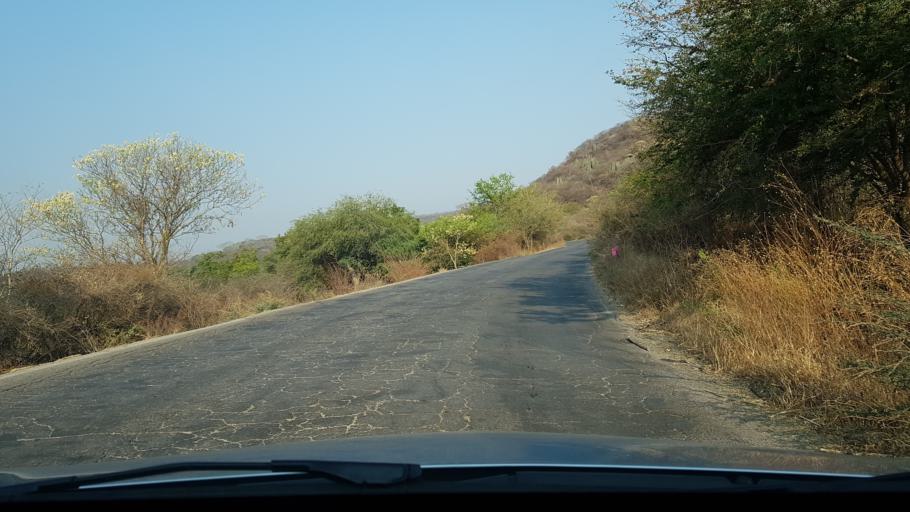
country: MX
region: Morelos
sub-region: Tepalcingo
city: Zacapalco
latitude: 18.6369
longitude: -99.0124
